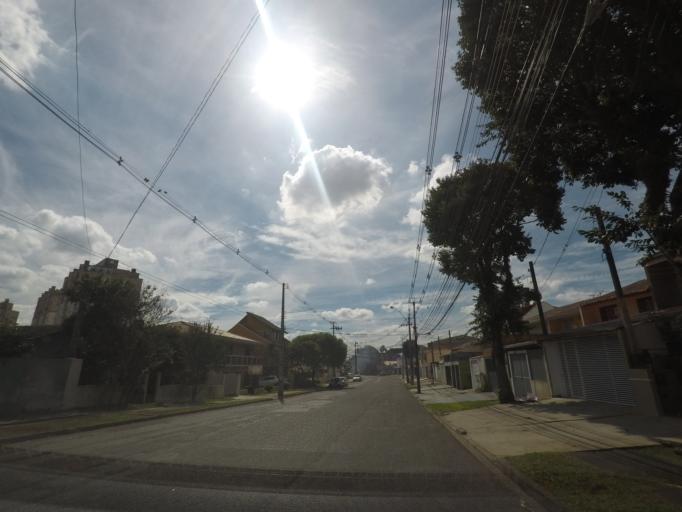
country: BR
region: Parana
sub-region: Curitiba
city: Curitiba
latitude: -25.4947
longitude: -49.2706
